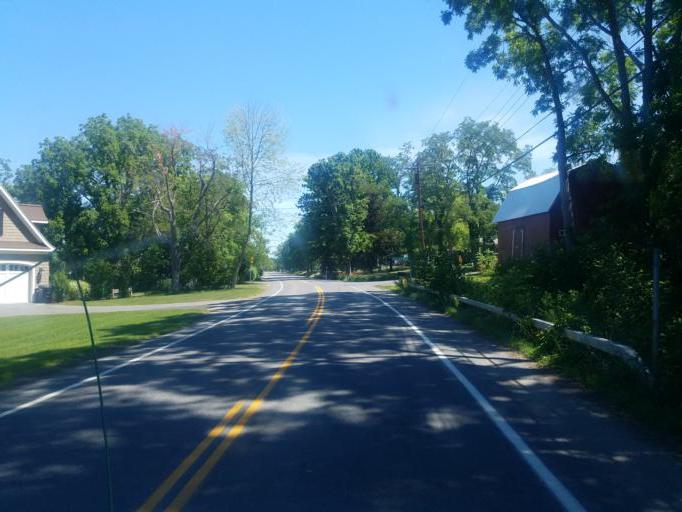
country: US
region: New York
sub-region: Ontario County
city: Canandaigua
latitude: 42.7920
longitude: -77.2743
